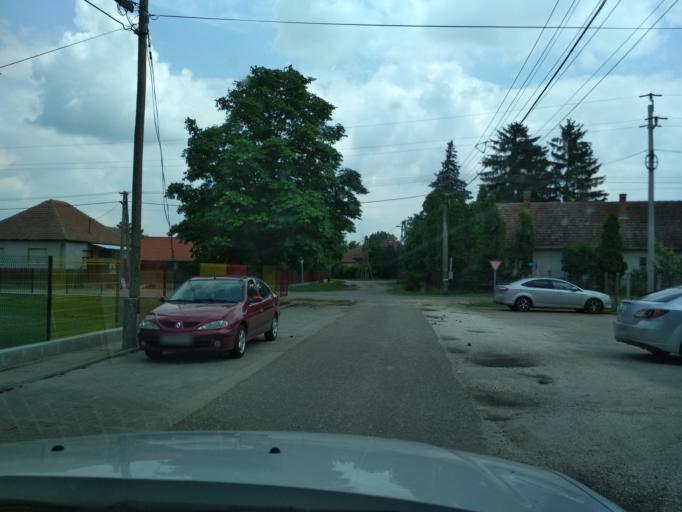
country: HU
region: Pest
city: Tapiobicske
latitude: 47.3598
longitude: 19.6852
